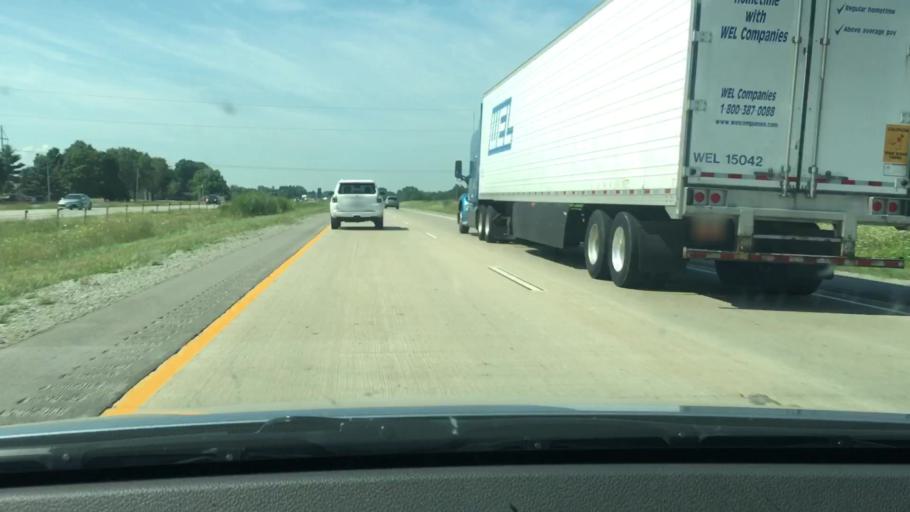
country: US
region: Wisconsin
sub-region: Brown County
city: Wrightstown
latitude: 44.4014
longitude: -88.1492
